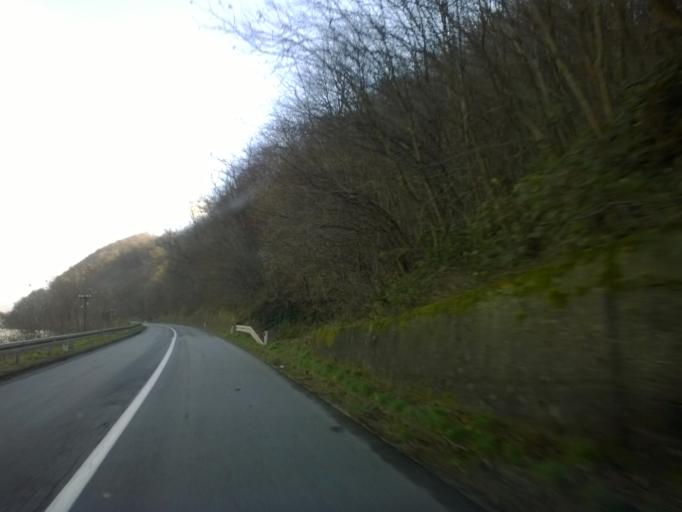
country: RS
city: Radenka
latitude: 44.6556
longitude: 21.7812
